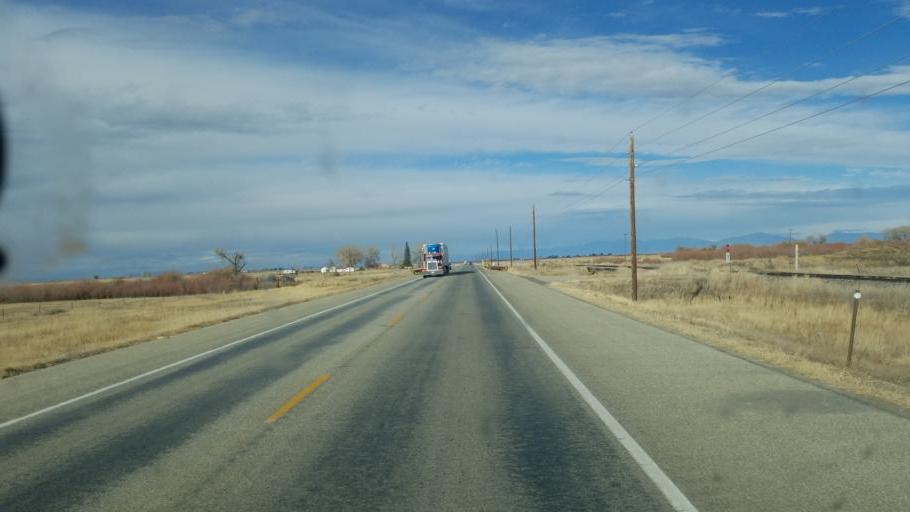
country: US
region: Colorado
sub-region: Alamosa County
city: Alamosa
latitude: 37.3069
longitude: -105.9527
